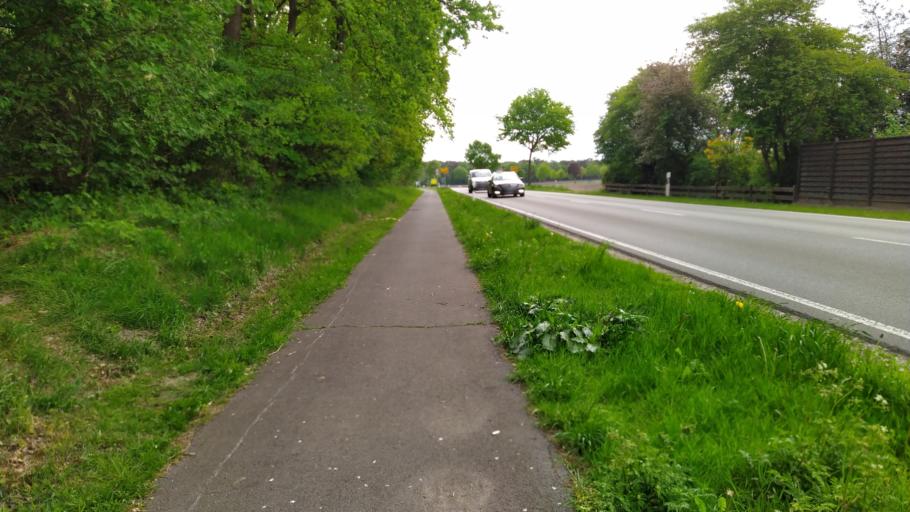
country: DE
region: Lower Saxony
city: Westertimke
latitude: 53.2358
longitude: 9.1275
